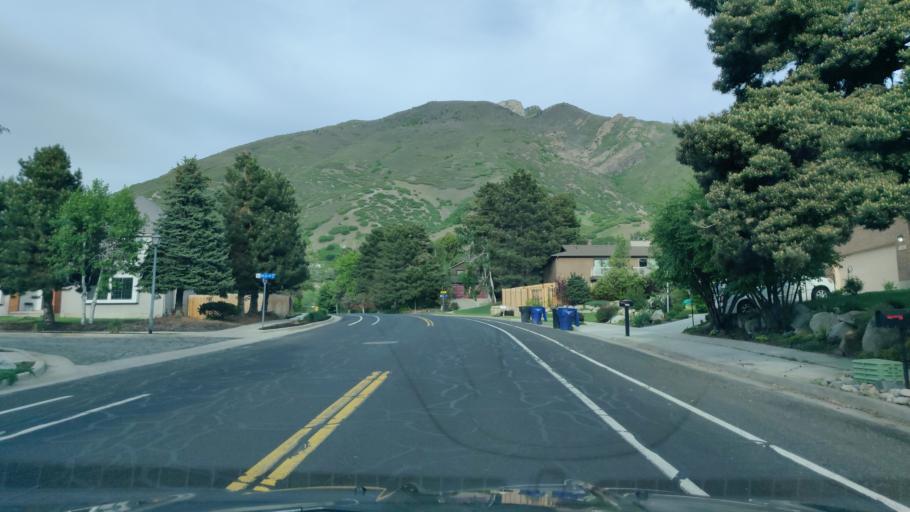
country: US
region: Utah
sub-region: Salt Lake County
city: Cottonwood Heights
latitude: 40.6044
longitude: -111.7991
